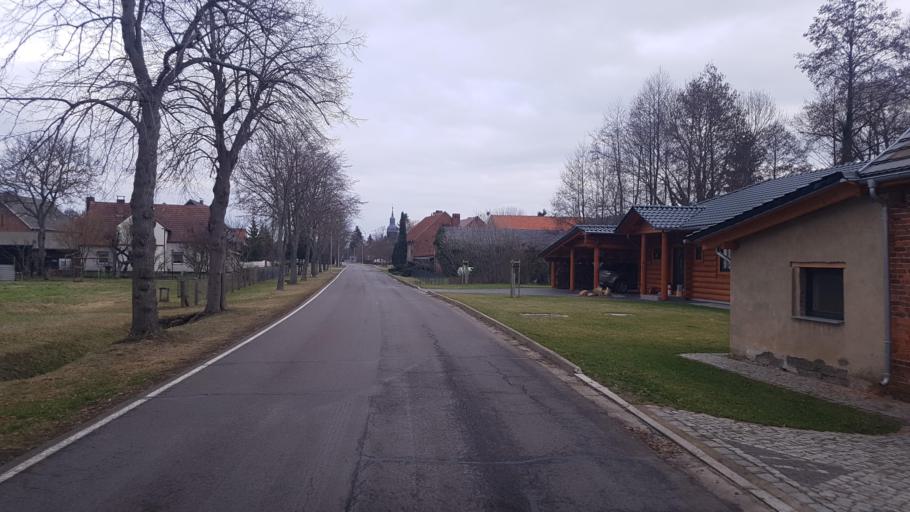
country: DE
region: Brandenburg
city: Drahnsdorf
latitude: 51.9230
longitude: 13.6310
